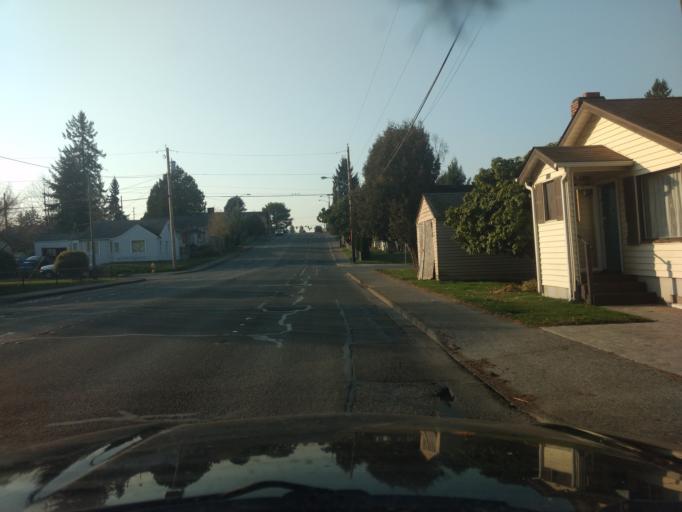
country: US
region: Washington
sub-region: Kitsap County
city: Bremerton
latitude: 47.5711
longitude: -122.6426
